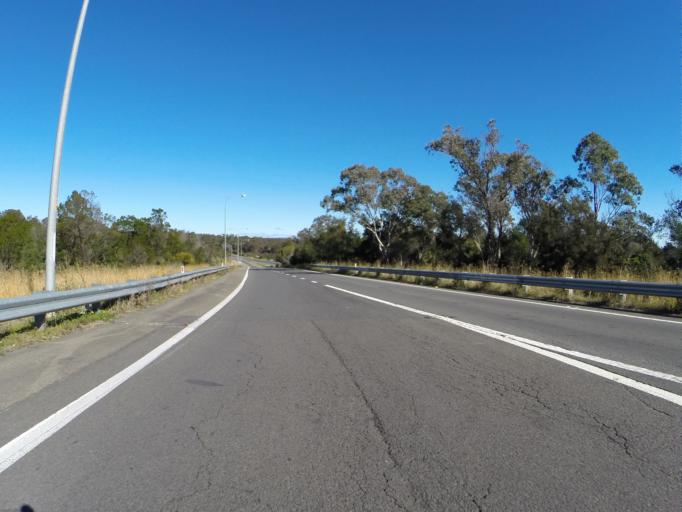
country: AU
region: New South Wales
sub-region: Wollondilly
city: Douglas Park
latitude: -34.2304
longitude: 150.6679
